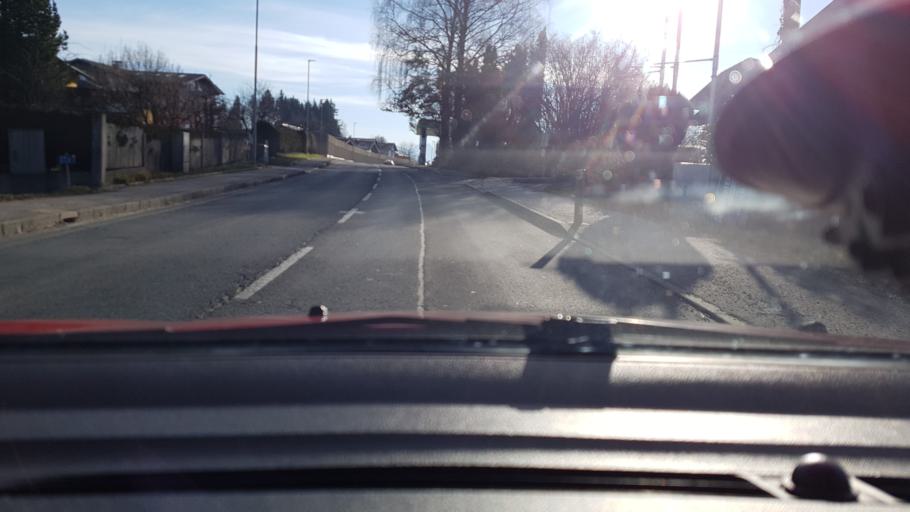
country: AT
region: Salzburg
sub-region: Politischer Bezirk Salzburg-Umgebung
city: Lamprechtshausen
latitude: 47.9874
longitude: 12.9546
